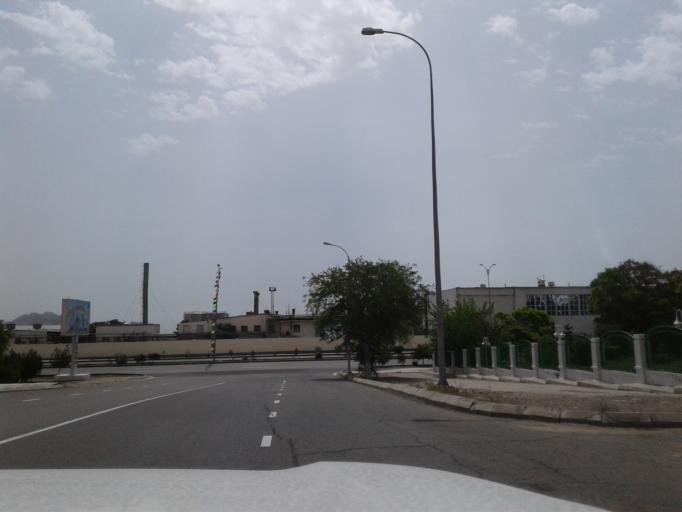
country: TM
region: Balkan
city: Turkmenbasy
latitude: 39.9987
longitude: 52.9923
